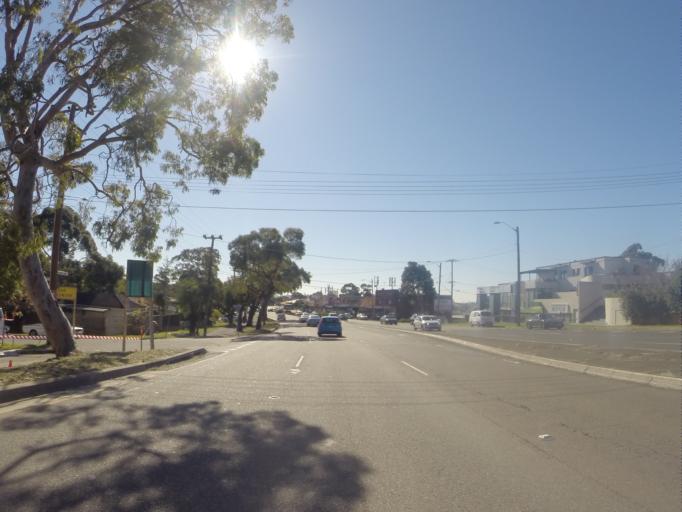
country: AU
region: New South Wales
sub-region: Sutherland Shire
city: Kareela
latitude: -34.0144
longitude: 151.0941
